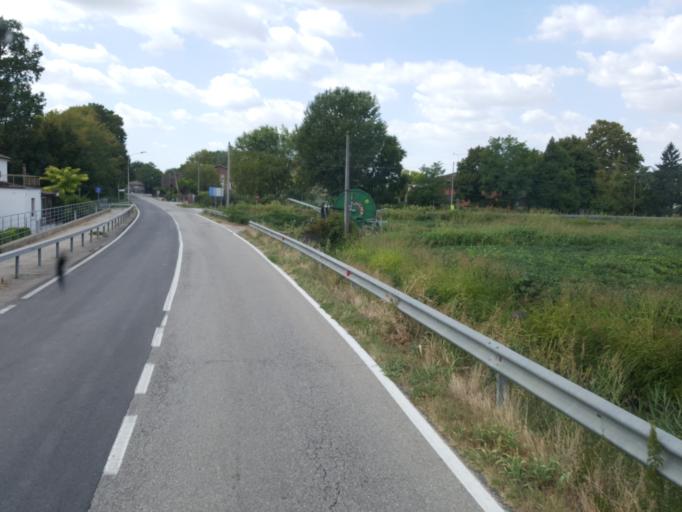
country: IT
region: Veneto
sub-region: Provincia di Verona
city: Roncanova
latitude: 45.1435
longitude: 11.0803
